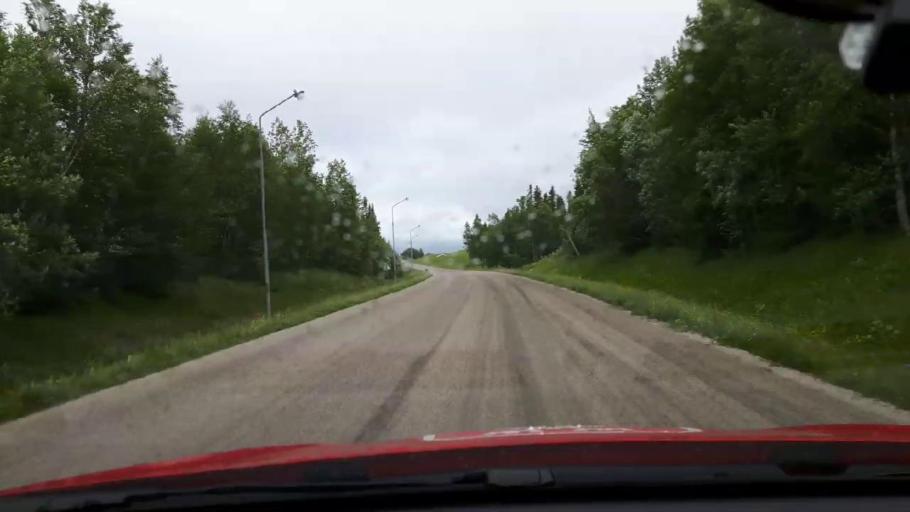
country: SE
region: Jaemtland
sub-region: Are Kommun
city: Are
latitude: 63.2605
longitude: 12.4209
